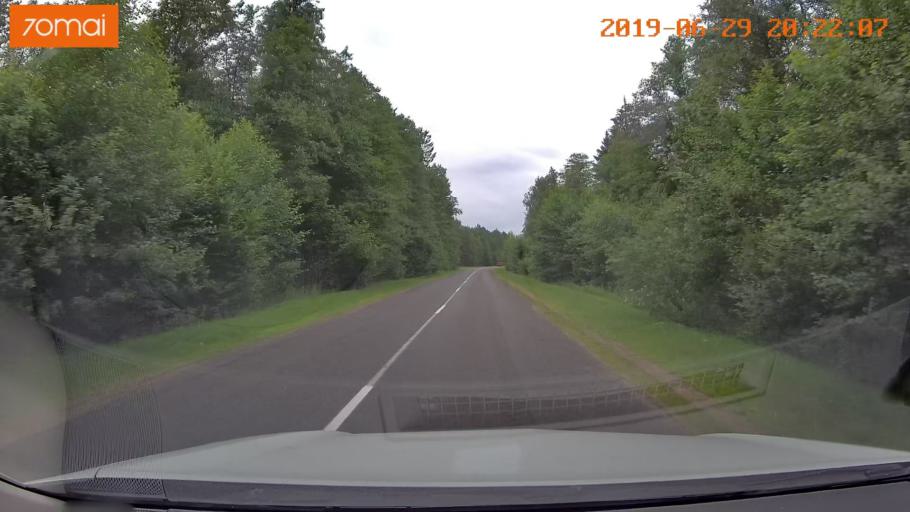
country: BY
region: Brest
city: Asnyezhytsy
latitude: 52.4279
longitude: 26.2536
